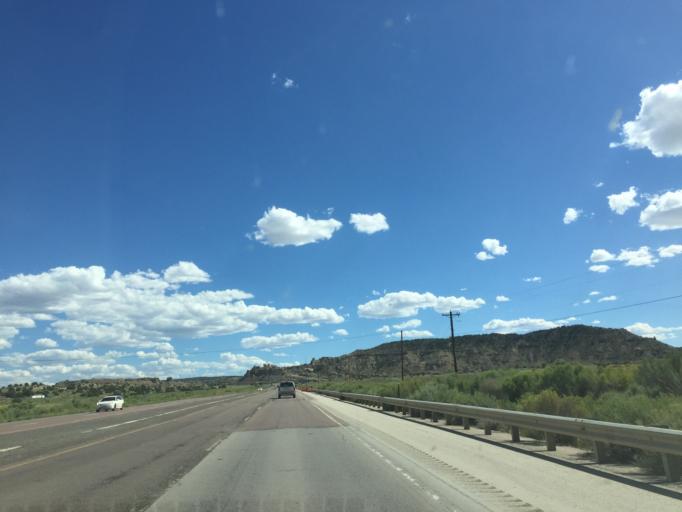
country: US
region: New Mexico
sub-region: McKinley County
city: Twin Lakes
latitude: 35.6799
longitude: -108.7740
